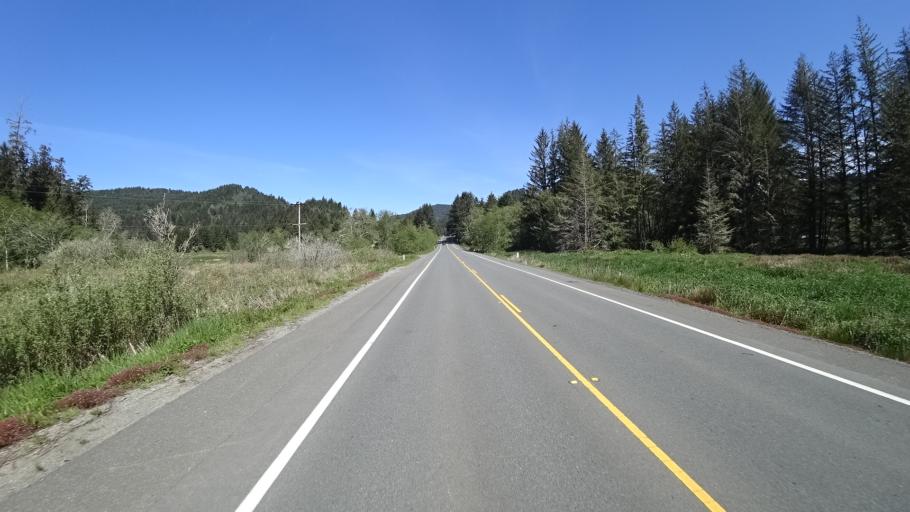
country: US
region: California
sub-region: Del Norte County
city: Bertsch-Oceanview
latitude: 41.5694
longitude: -124.0697
